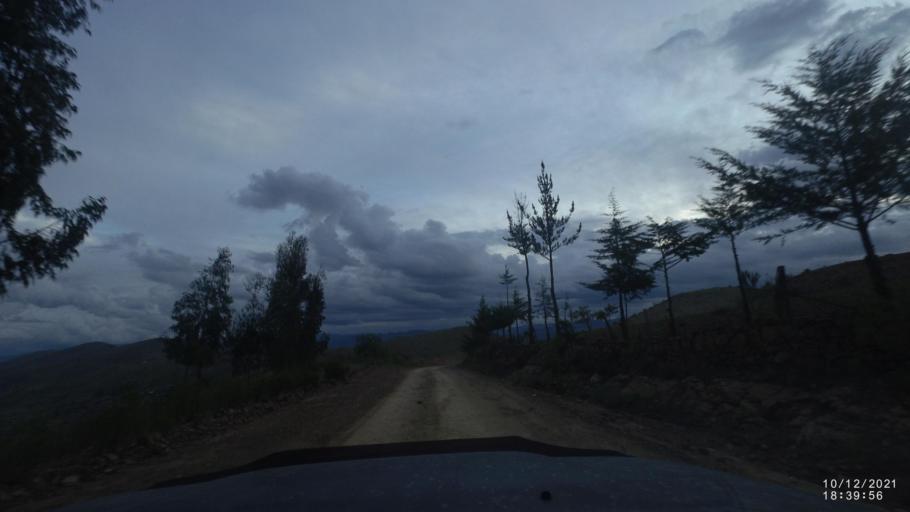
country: BO
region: Cochabamba
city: Tarata
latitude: -17.8538
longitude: -65.9881
